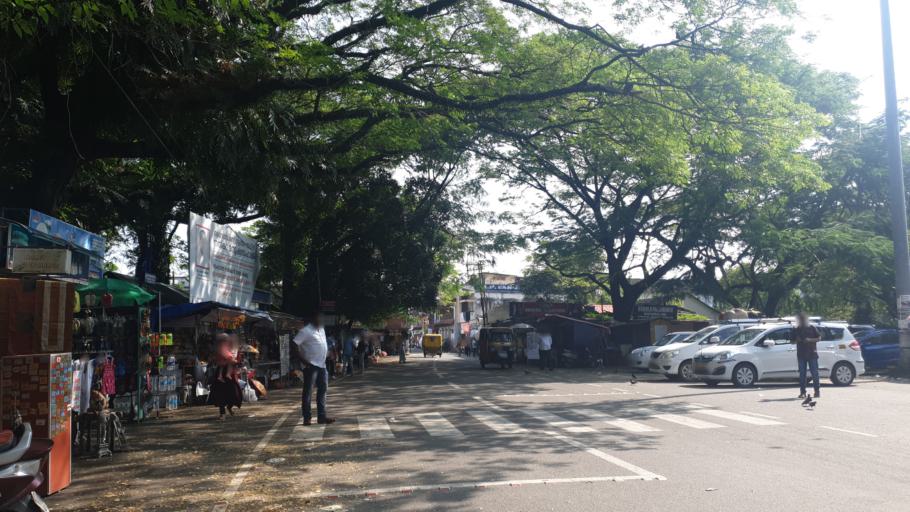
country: IN
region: Kerala
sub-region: Ernakulam
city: Cochin
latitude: 9.9583
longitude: 76.2600
